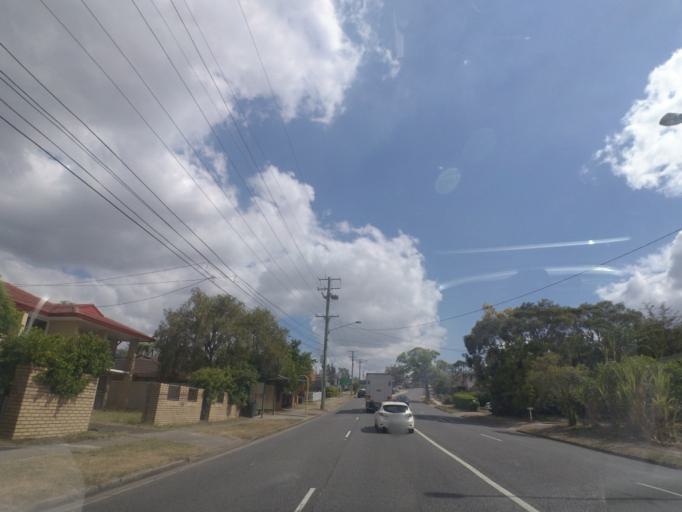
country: AU
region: Queensland
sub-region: Brisbane
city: Upper Mount Gravatt
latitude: -27.5575
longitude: 153.0897
